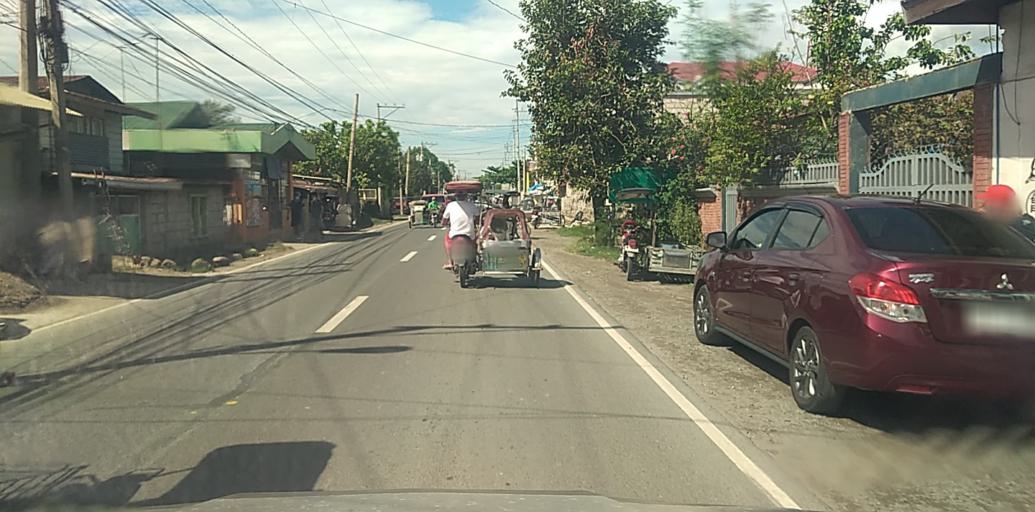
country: PH
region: Central Luzon
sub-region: Province of Pampanga
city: Arayat
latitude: 15.1470
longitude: 120.7638
